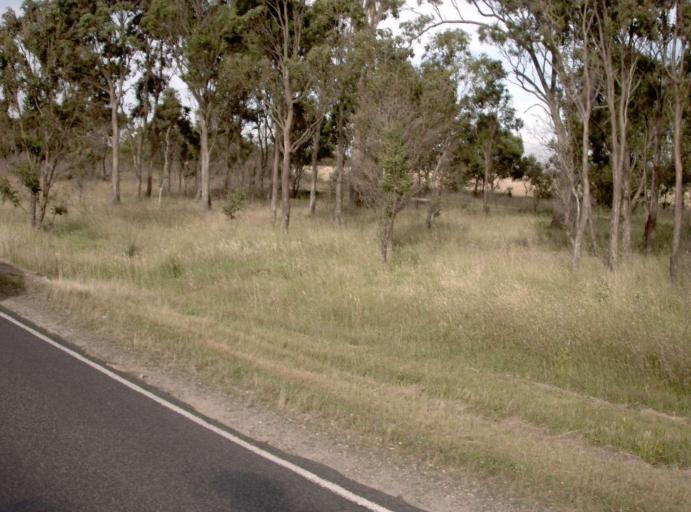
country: AU
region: Victoria
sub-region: Latrobe
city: Traralgon
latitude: -38.0720
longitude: 146.6139
